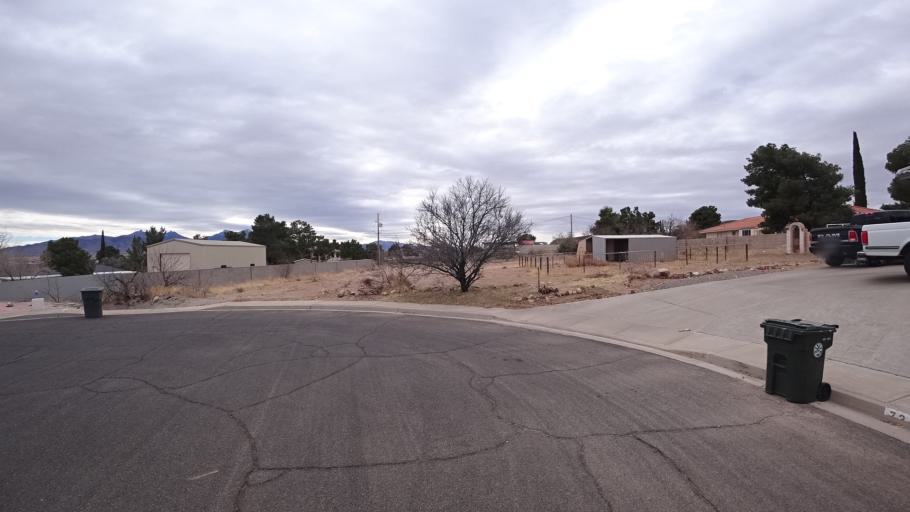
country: US
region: Arizona
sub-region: Mohave County
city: New Kingman-Butler
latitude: 35.2369
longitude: -114.0472
